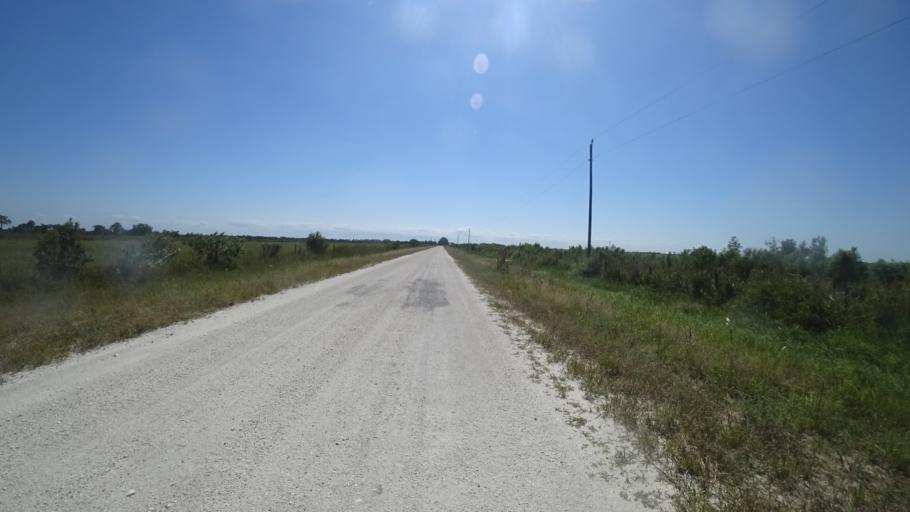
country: US
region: Florida
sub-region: DeSoto County
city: Arcadia
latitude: 27.3357
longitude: -82.0806
